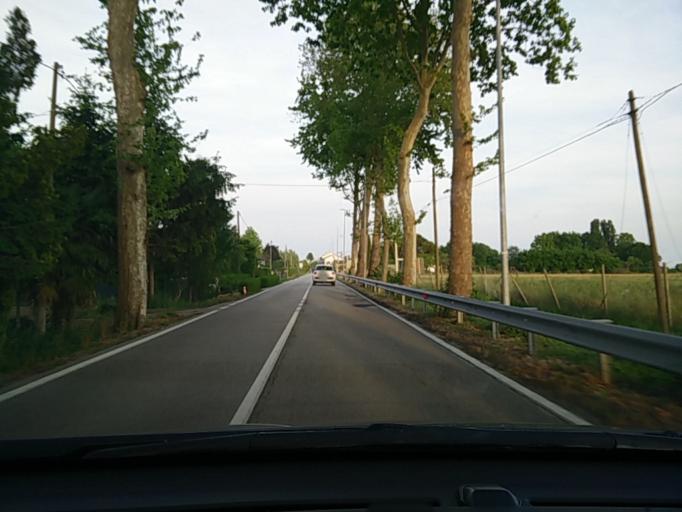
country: IT
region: Veneto
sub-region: Provincia di Venezia
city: Quarto d'Altino
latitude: 45.5654
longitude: 12.4014
